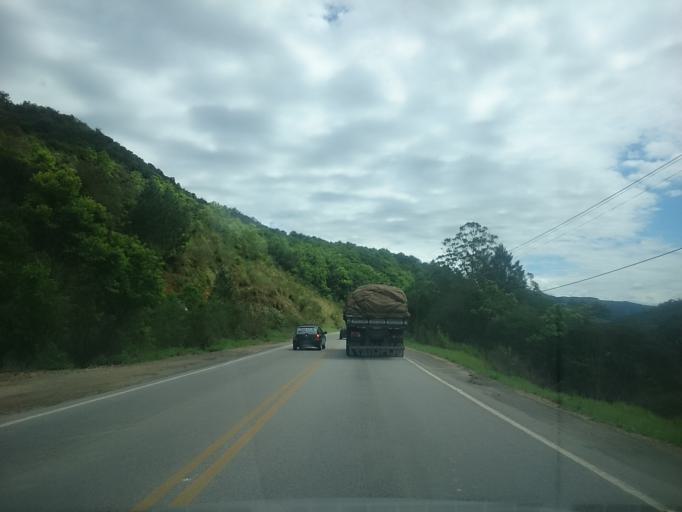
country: BR
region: Santa Catarina
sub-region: Anitapolis
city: Anitapolis
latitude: -27.6944
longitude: -49.3132
